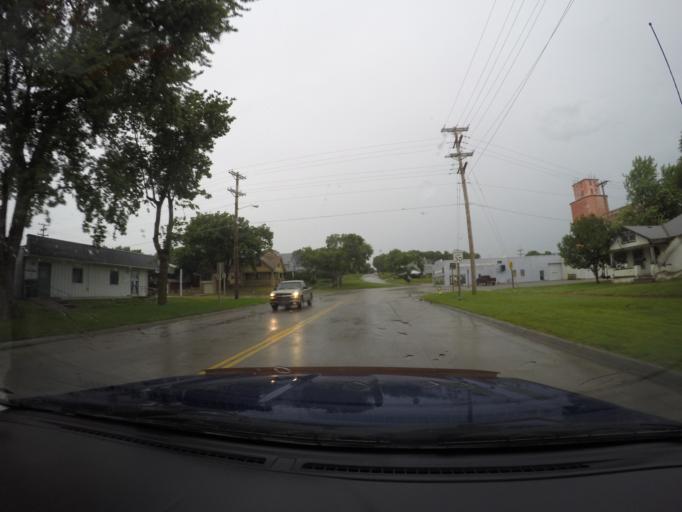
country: US
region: Kansas
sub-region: Cloud County
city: Concordia
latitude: 39.5726
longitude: -97.6644
